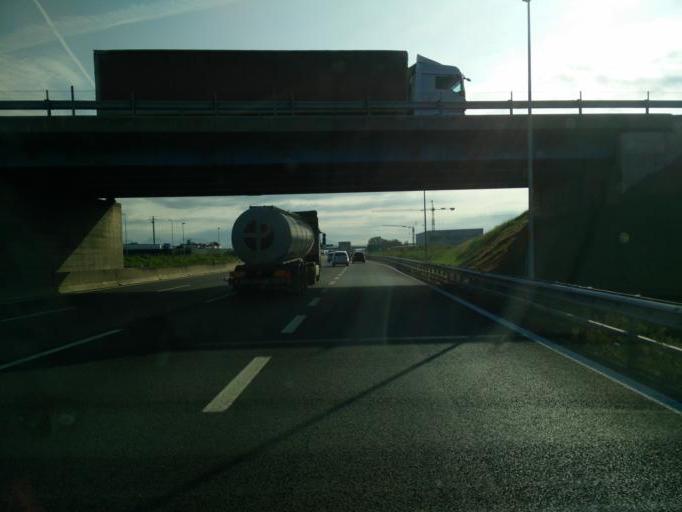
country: IT
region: Lombardy
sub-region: Provincia di Brescia
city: Rovato
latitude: 45.5769
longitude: 10.0078
